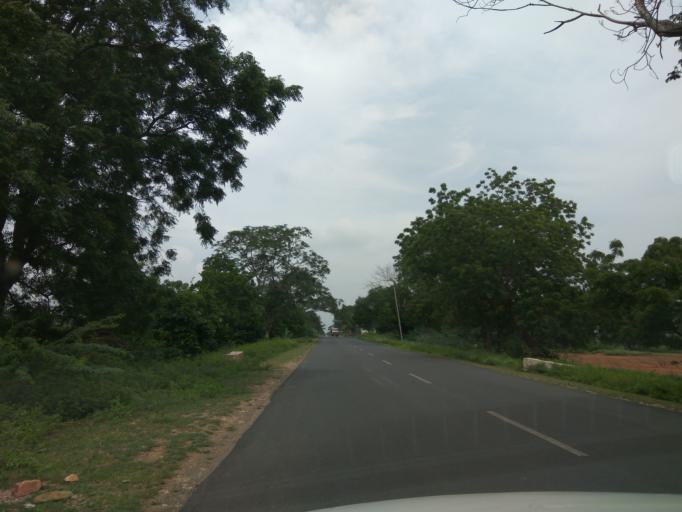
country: IN
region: Andhra Pradesh
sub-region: Prakasam
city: Cumbum
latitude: 15.5014
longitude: 79.0849
